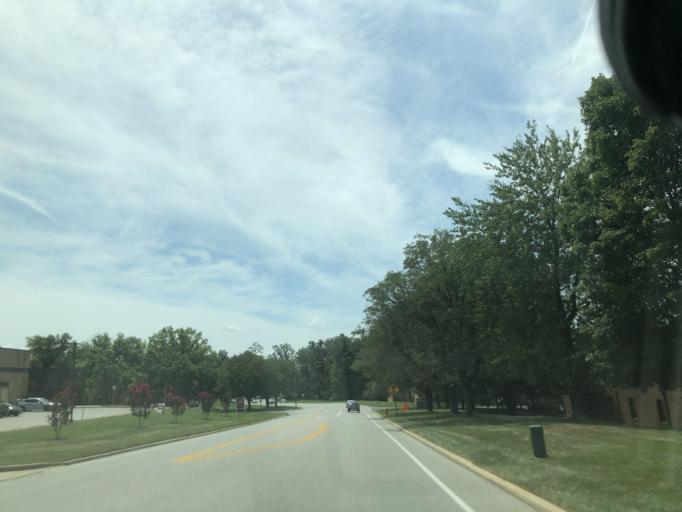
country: US
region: Maryland
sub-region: Howard County
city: Savage
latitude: 39.1867
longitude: -76.8253
